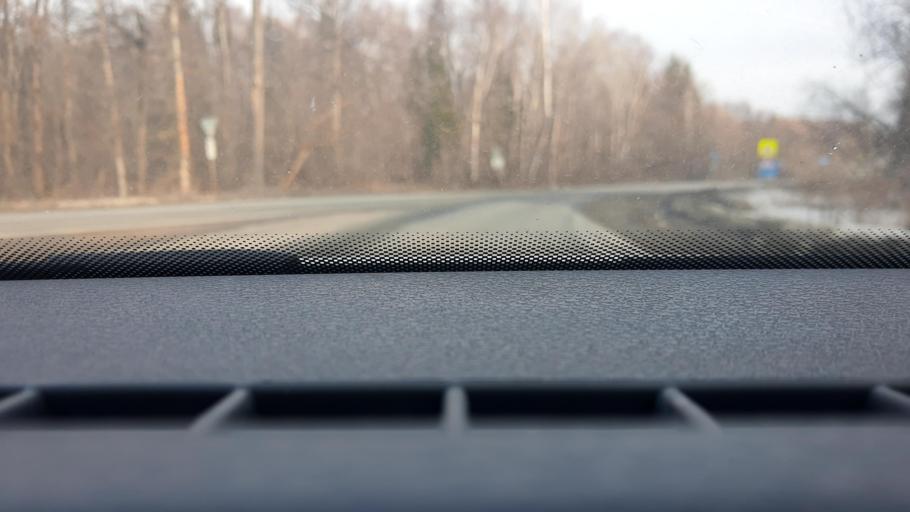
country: RU
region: Chelyabinsk
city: Asha
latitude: 54.8889
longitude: 57.3006
